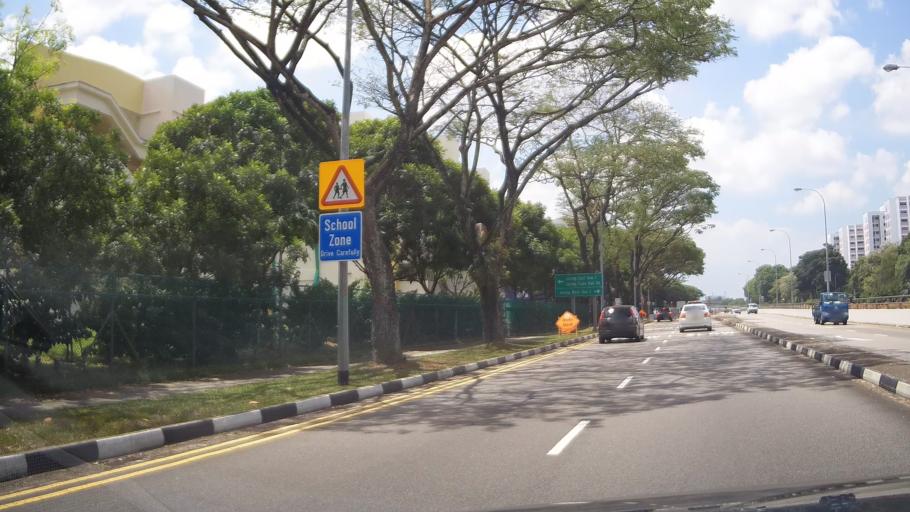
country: MY
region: Johor
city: Johor Bahru
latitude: 1.3522
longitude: 103.7283
